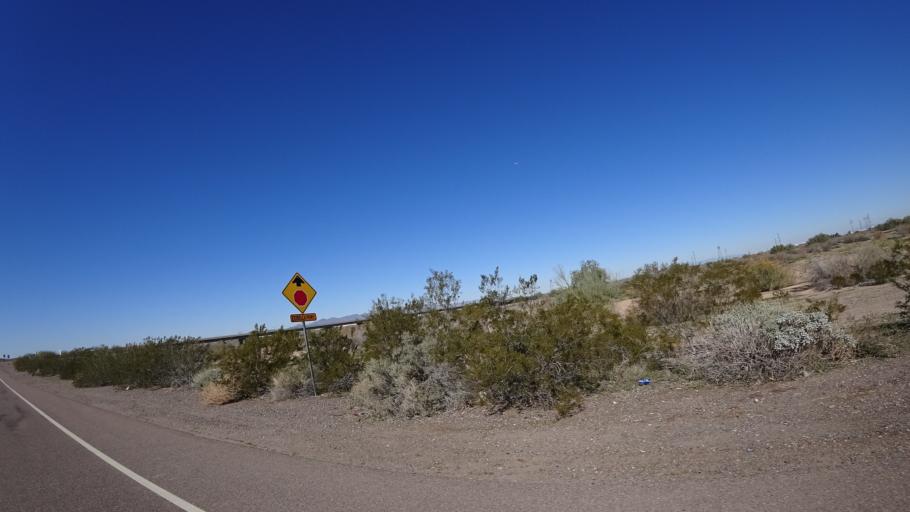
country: US
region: Arizona
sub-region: Maricopa County
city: Goodyear
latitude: 33.3880
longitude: -112.3897
